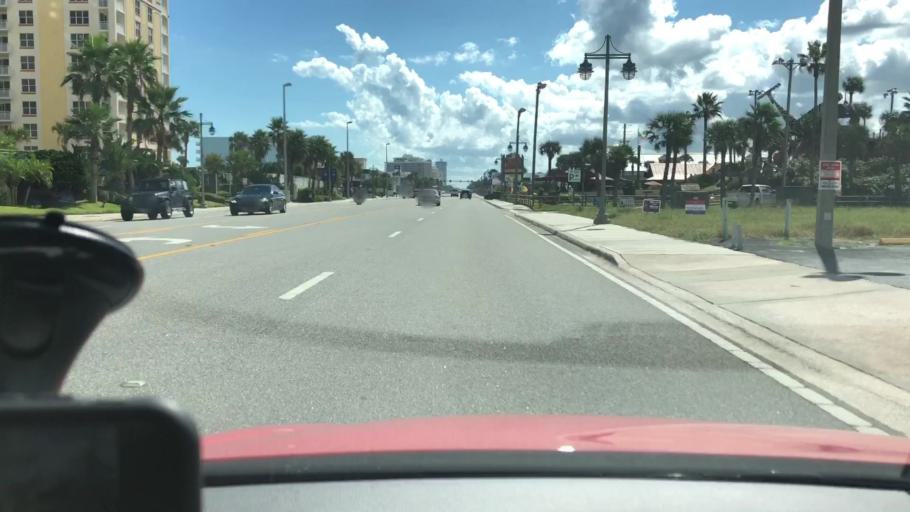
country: US
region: Florida
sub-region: Volusia County
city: Daytona Beach Shores
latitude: 29.1996
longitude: -80.9949
